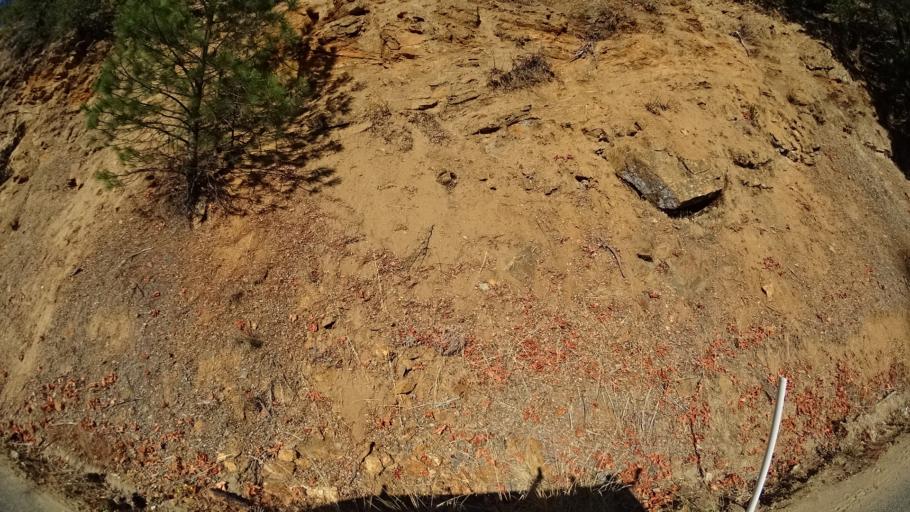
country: US
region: California
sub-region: Siskiyou County
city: Happy Camp
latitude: 41.6342
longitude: -123.1005
